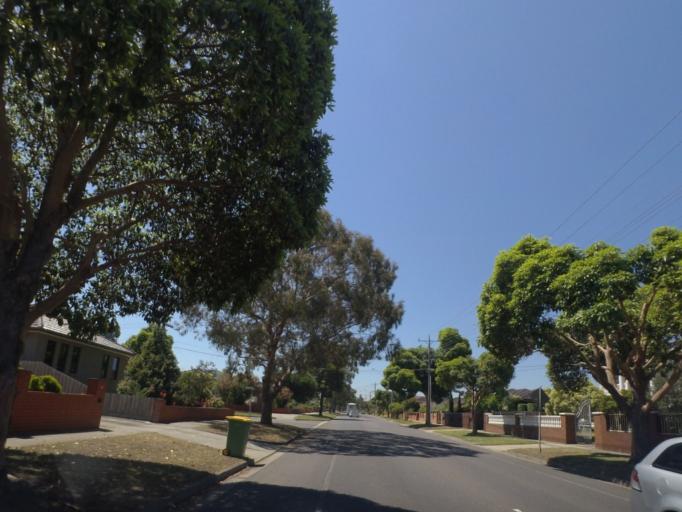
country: AU
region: Victoria
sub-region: Darebin
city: Reservoir
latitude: -37.7013
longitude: 144.9897
